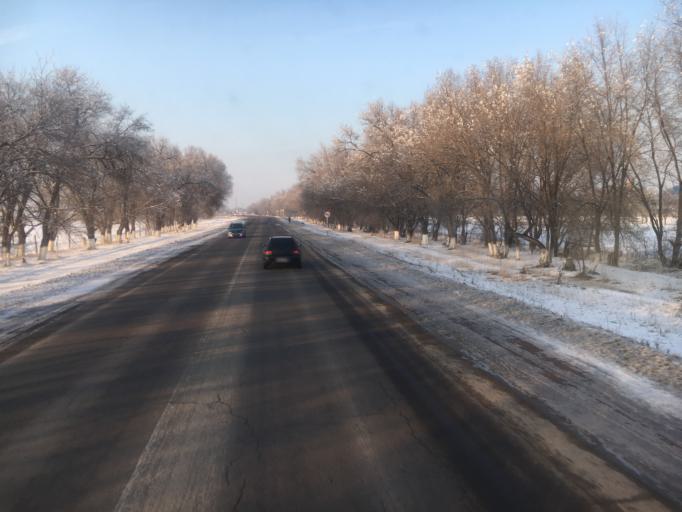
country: KZ
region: Almaty Oblysy
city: Burunday
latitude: 43.3283
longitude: 76.6623
